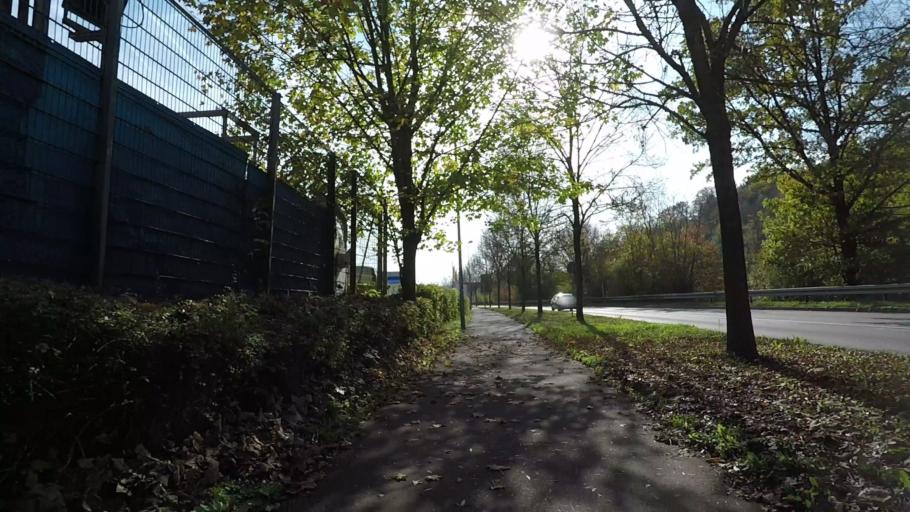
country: DE
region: Baden-Wuerttemberg
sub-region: Tuebingen Region
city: Wannweil
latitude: 48.5235
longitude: 9.1447
